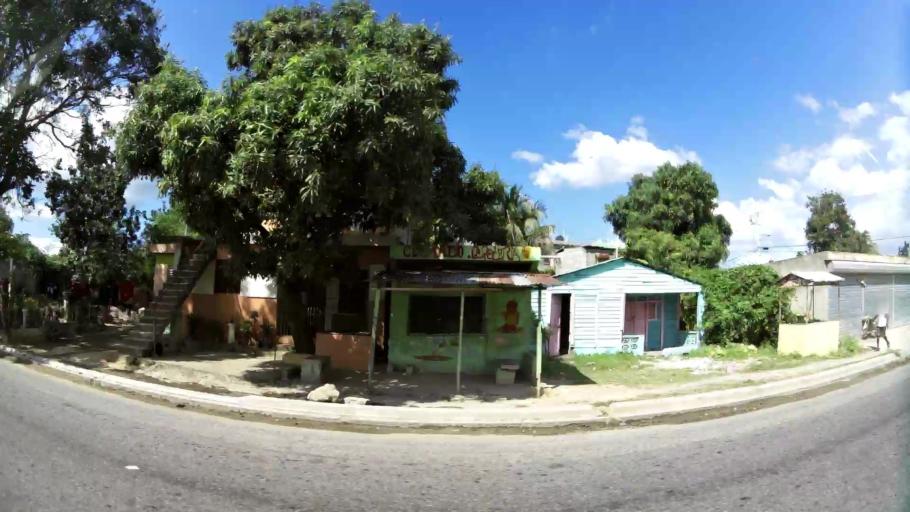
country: DO
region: San Cristobal
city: San Cristobal
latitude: 18.4250
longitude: -70.0713
